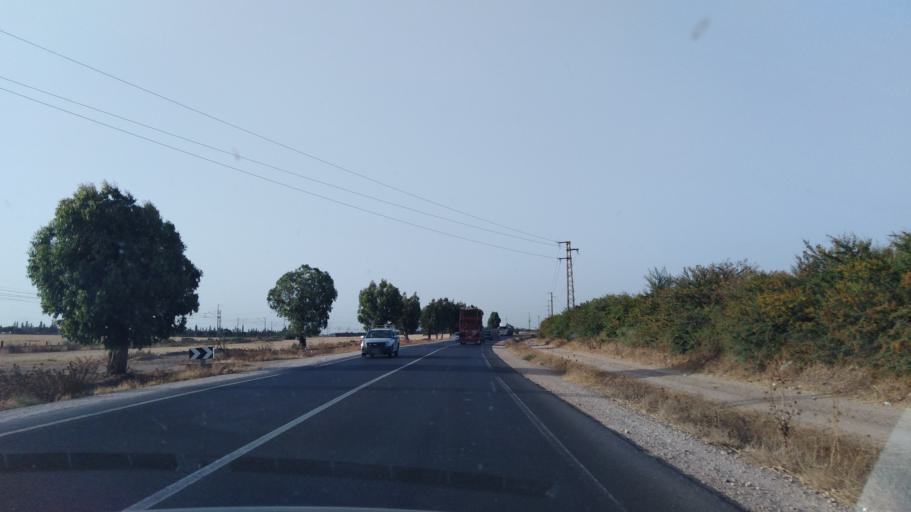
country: MA
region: Chaouia-Ouardigha
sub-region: Settat Province
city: Berrechid
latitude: 33.1374
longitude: -7.6253
